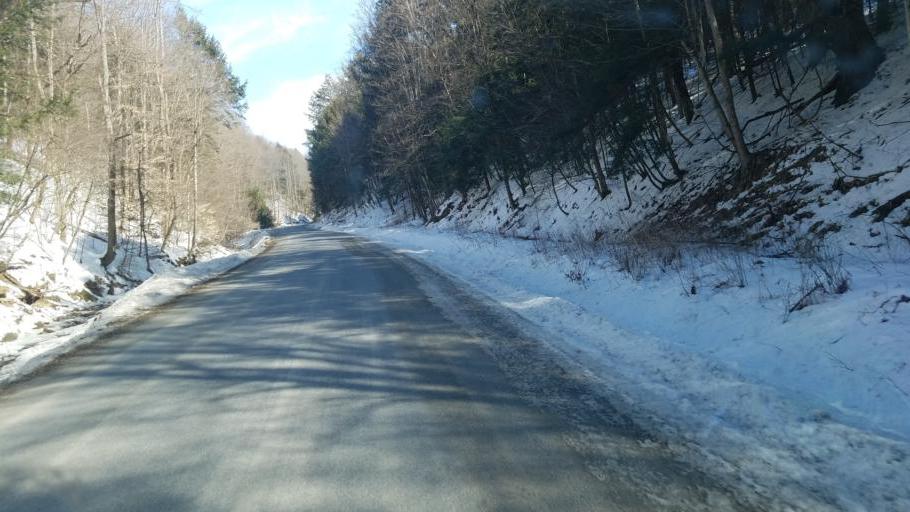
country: US
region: New York
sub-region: Allegany County
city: Andover
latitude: 42.0451
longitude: -77.7792
